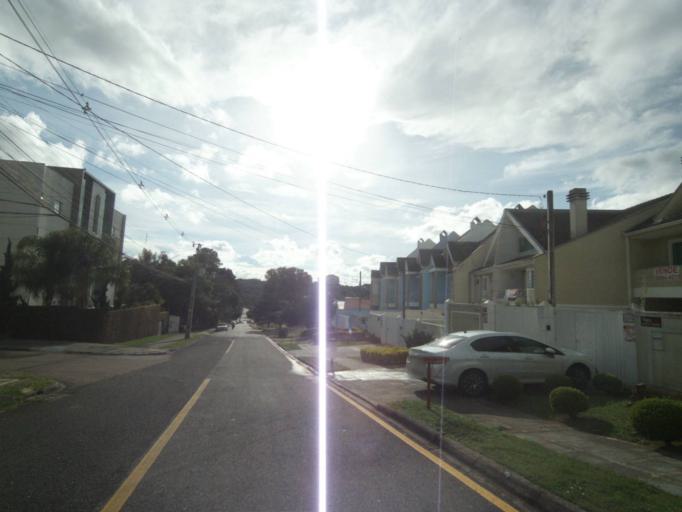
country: BR
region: Parana
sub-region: Curitiba
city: Curitiba
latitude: -25.4421
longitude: -49.3103
